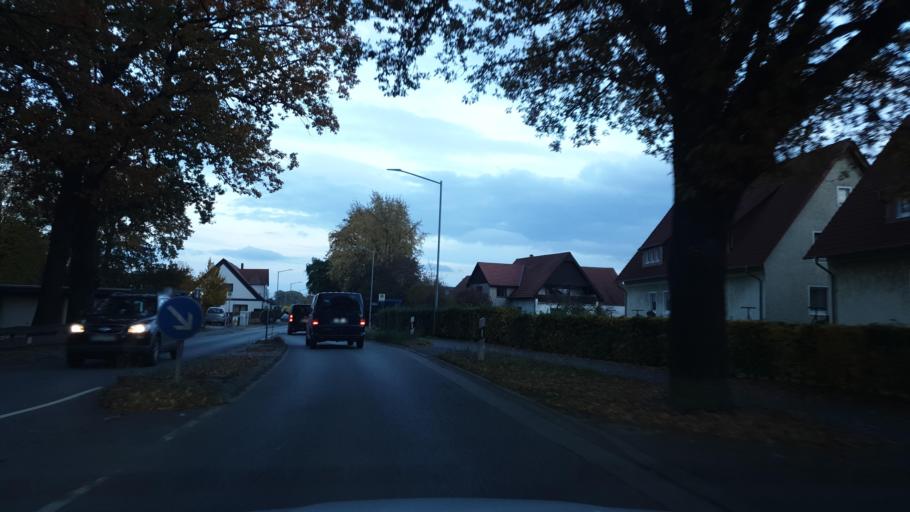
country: DE
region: North Rhine-Westphalia
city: Buende
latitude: 52.1928
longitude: 8.5284
